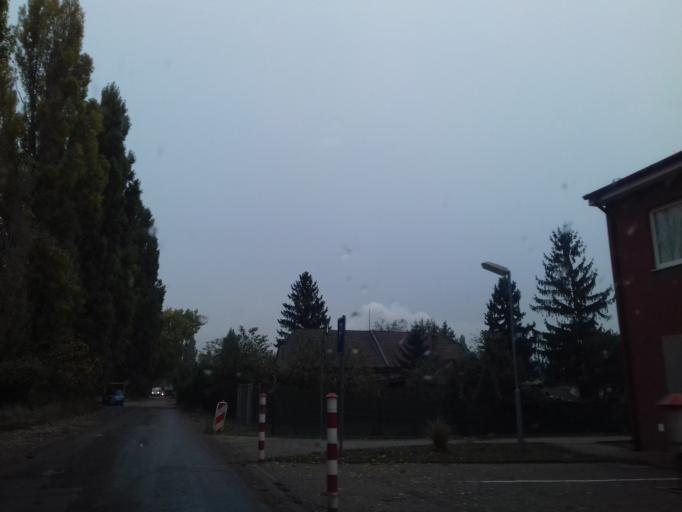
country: SK
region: Bratislavsky
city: Bratislava
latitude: 48.1366
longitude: 17.1721
